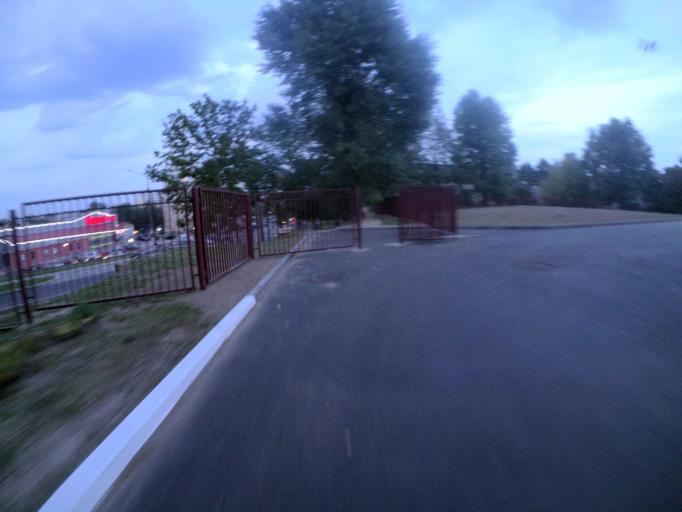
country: BY
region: Grodnenskaya
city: Hrodna
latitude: 53.6969
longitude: 23.8276
